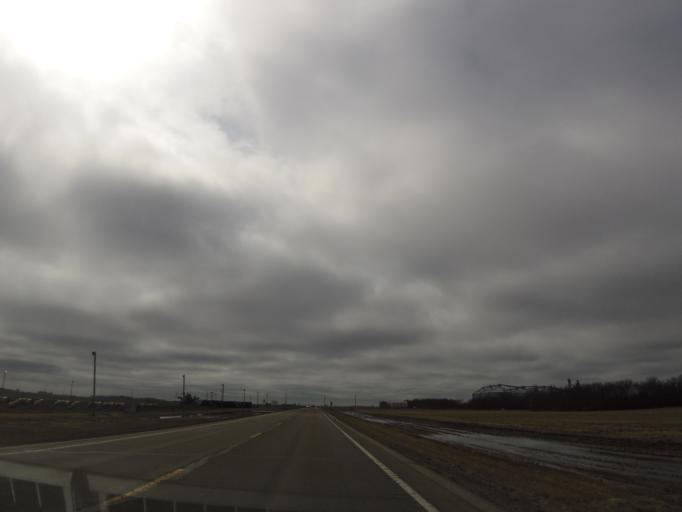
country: US
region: North Dakota
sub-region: Cass County
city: Casselton
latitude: 47.0103
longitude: -97.2138
